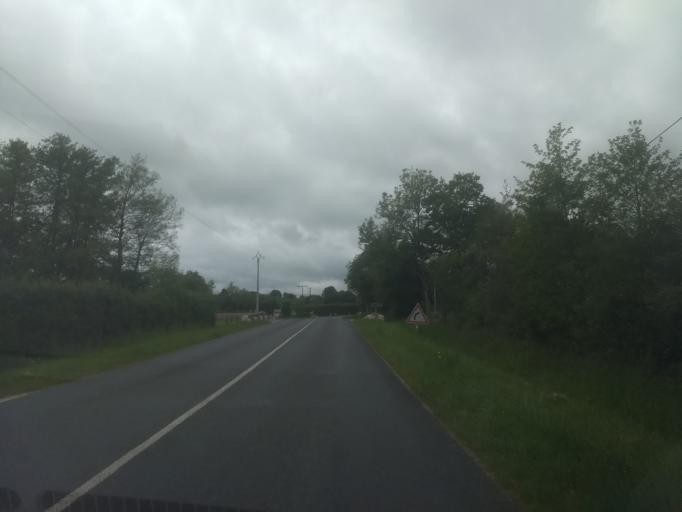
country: FR
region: Centre
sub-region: Departement d'Eure-et-Loir
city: La Loupe
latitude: 48.5054
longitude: 1.0324
